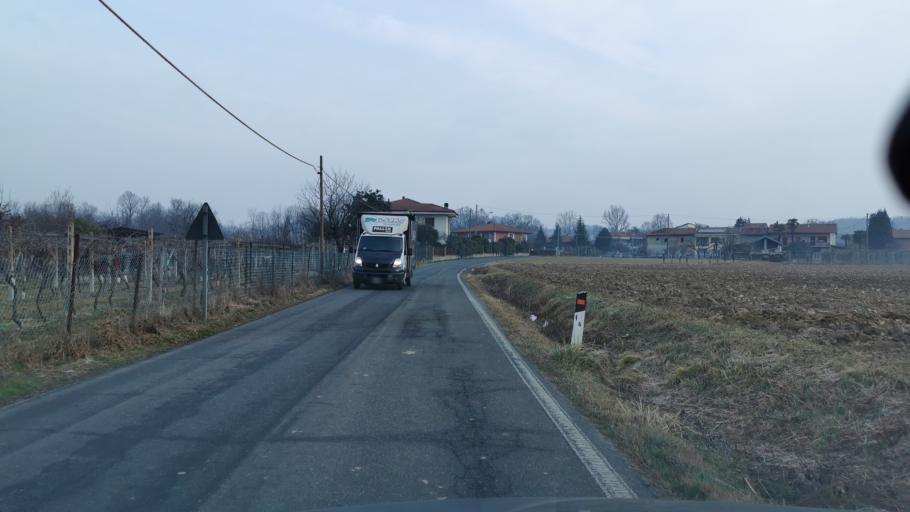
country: IT
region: Piedmont
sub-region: Provincia di Torino
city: Cuceglio
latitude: 45.3484
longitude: 7.8119
